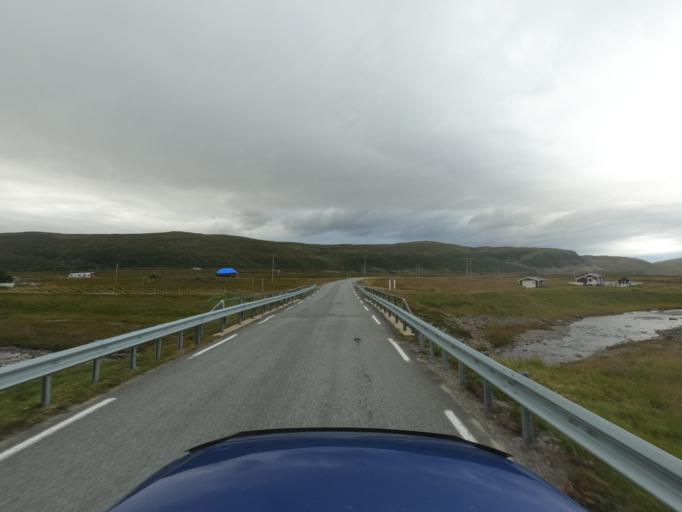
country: NO
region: Finnmark Fylke
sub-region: Nordkapp
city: Honningsvag
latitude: 70.7499
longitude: 25.5906
